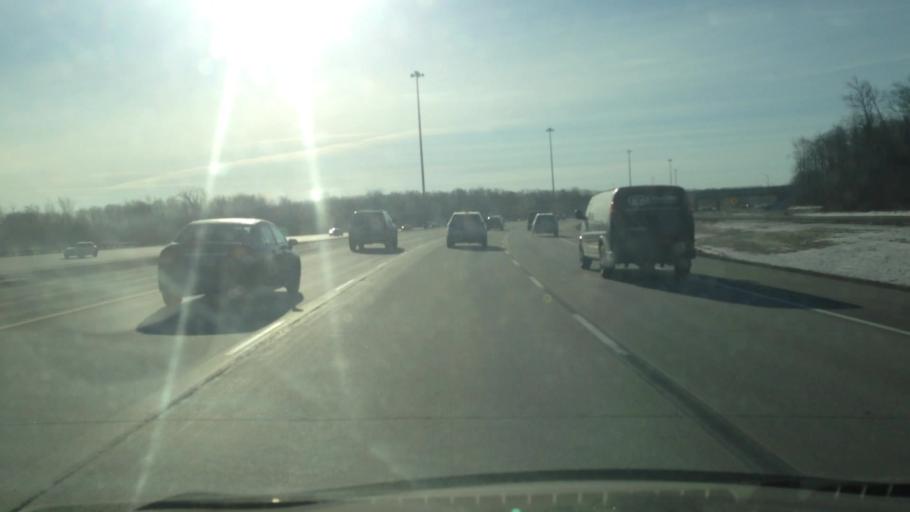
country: CA
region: Quebec
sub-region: Laurentides
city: Saint-Jerome
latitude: 45.7243
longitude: -73.9710
